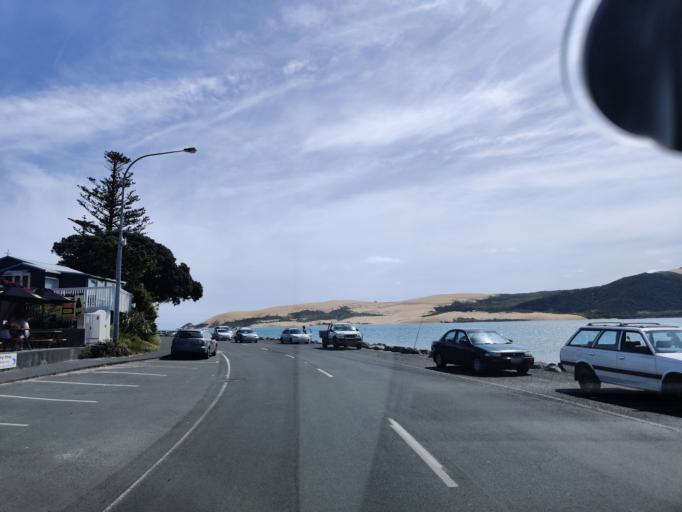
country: NZ
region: Northland
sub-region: Far North District
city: Ahipara
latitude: -35.5045
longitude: 173.3916
